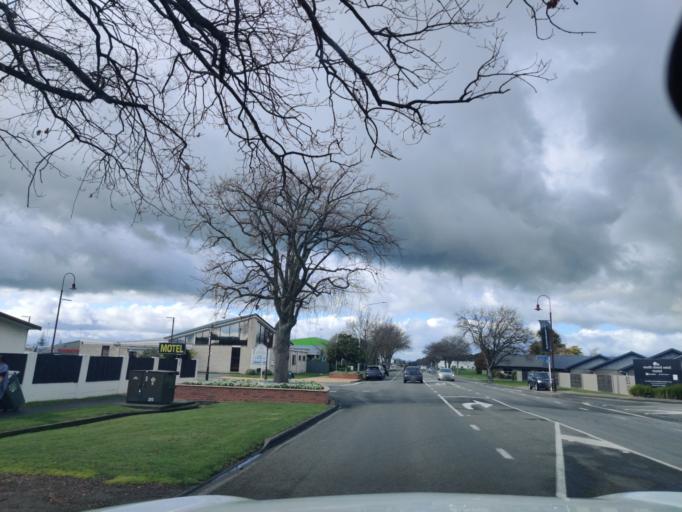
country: NZ
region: Manawatu-Wanganui
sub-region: Palmerston North City
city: Palmerston North
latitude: -40.2295
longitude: 175.5612
